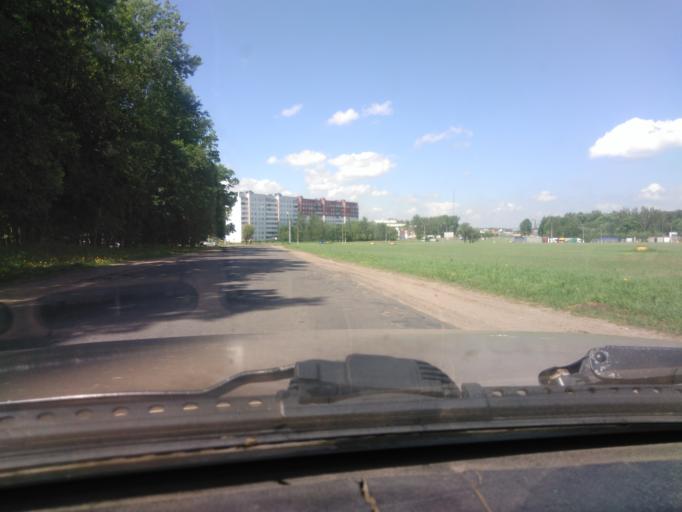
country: BY
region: Mogilev
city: Palykavichy Pyershyya
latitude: 53.9550
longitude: 30.3664
